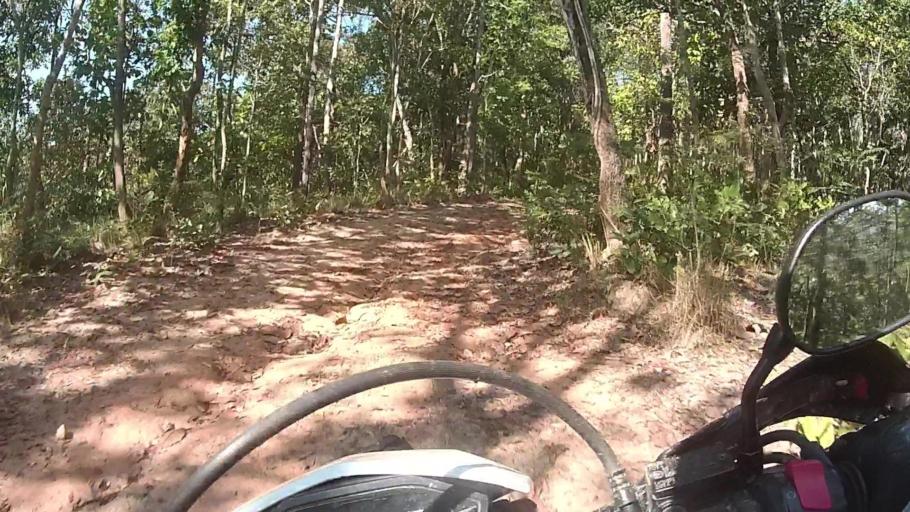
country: TH
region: Chiang Mai
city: Mae On
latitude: 19.0213
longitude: 99.3029
